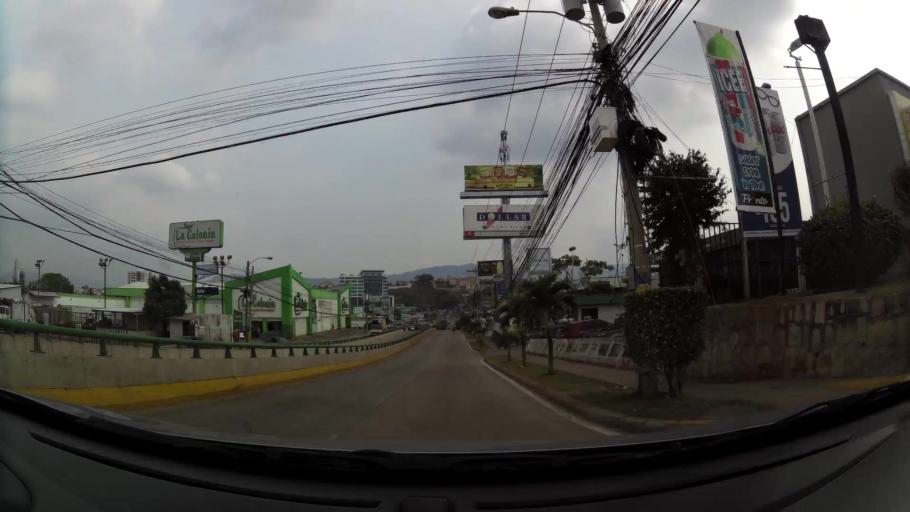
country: HN
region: Francisco Morazan
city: Tegucigalpa
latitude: 14.0846
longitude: -87.1737
